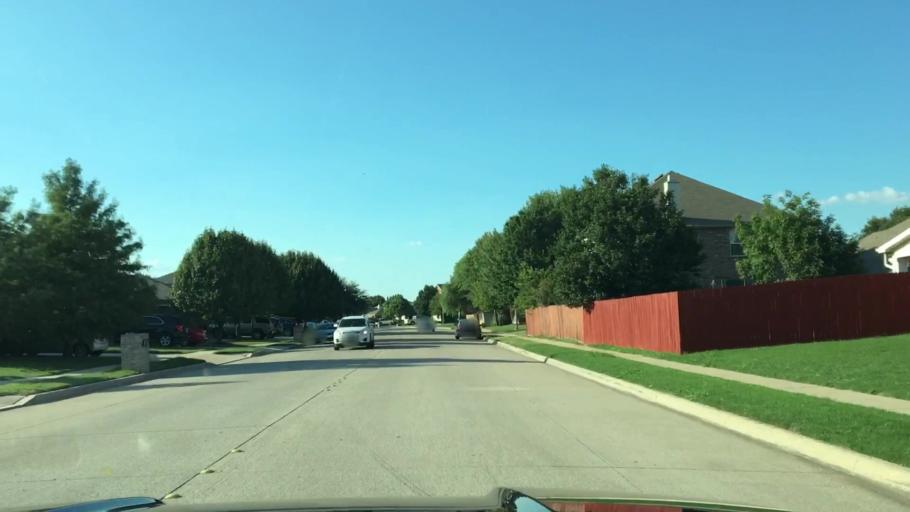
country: US
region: Texas
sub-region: Denton County
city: Justin
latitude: 33.0381
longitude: -97.3194
